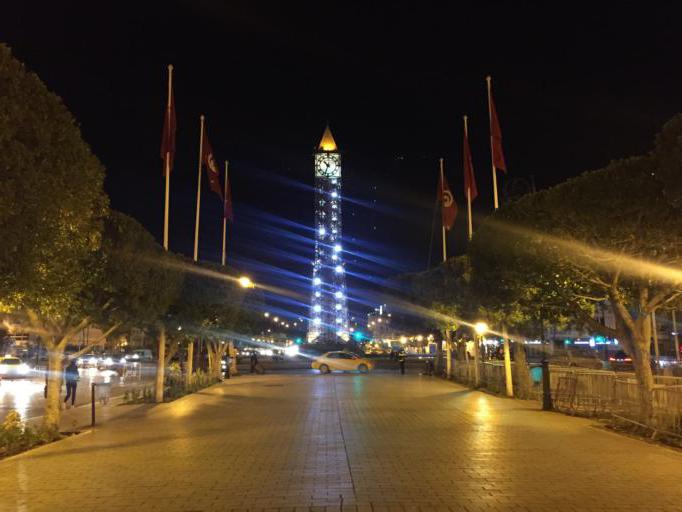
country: TN
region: Tunis
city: Tunis
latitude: 36.8003
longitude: 10.1854
